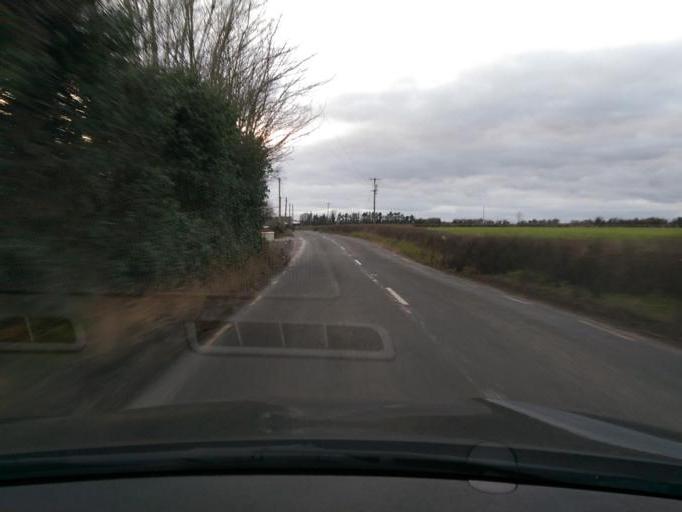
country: IE
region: Leinster
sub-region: Uibh Fhaili
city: Banagher
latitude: 53.1083
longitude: -8.0708
